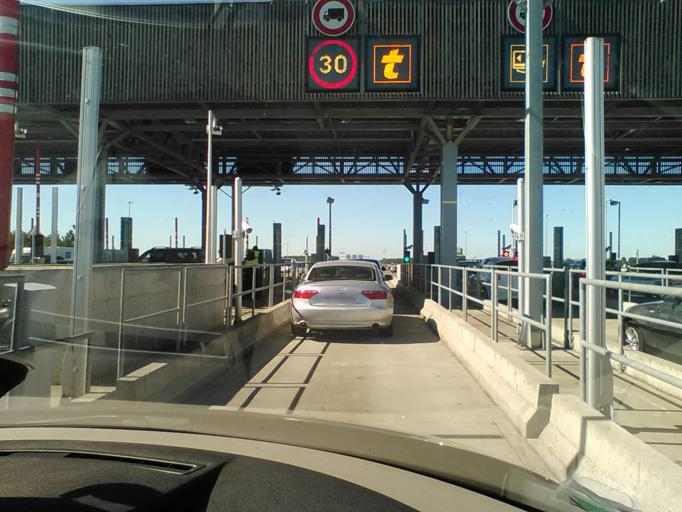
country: FR
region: Aquitaine
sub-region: Departement des Landes
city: Pissos
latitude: 44.3472
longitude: -0.8602
